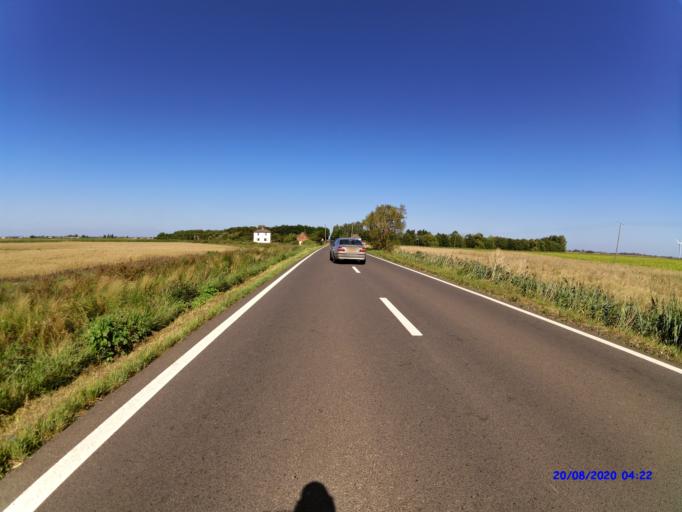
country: GB
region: England
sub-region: Cambridgeshire
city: Ramsey
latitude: 52.4959
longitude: -0.1233
